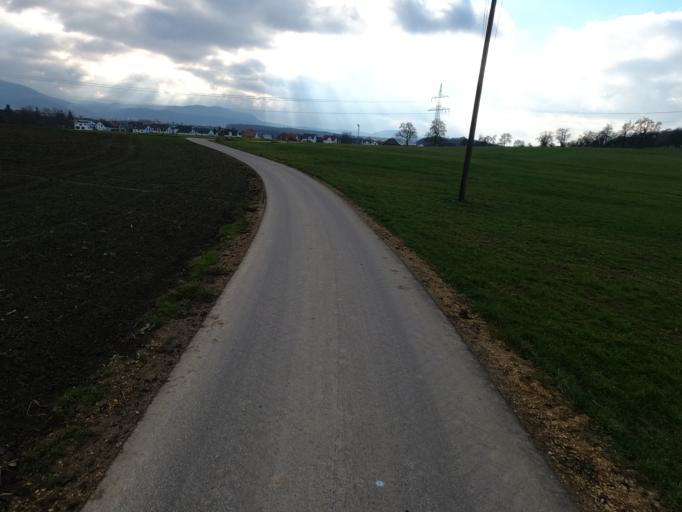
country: DE
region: Baden-Wuerttemberg
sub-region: Regierungsbezirk Stuttgart
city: Boll
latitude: 48.6774
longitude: 9.6103
